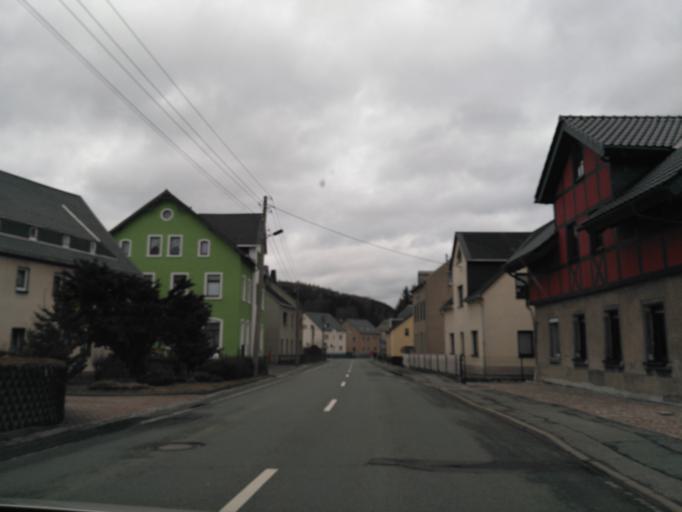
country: DE
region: Saxony
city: Thum
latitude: 50.6748
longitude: 12.9757
